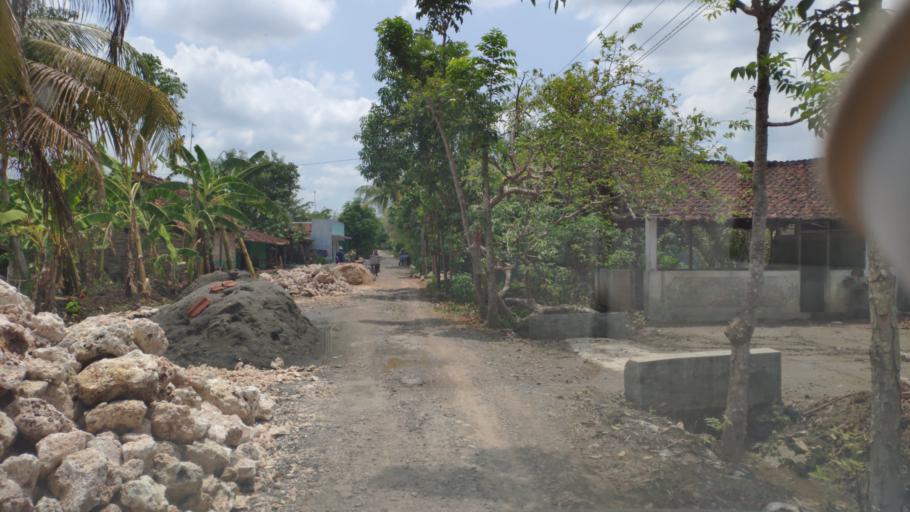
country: ID
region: Central Java
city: Ngablak
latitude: -7.0277
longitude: 111.3879
